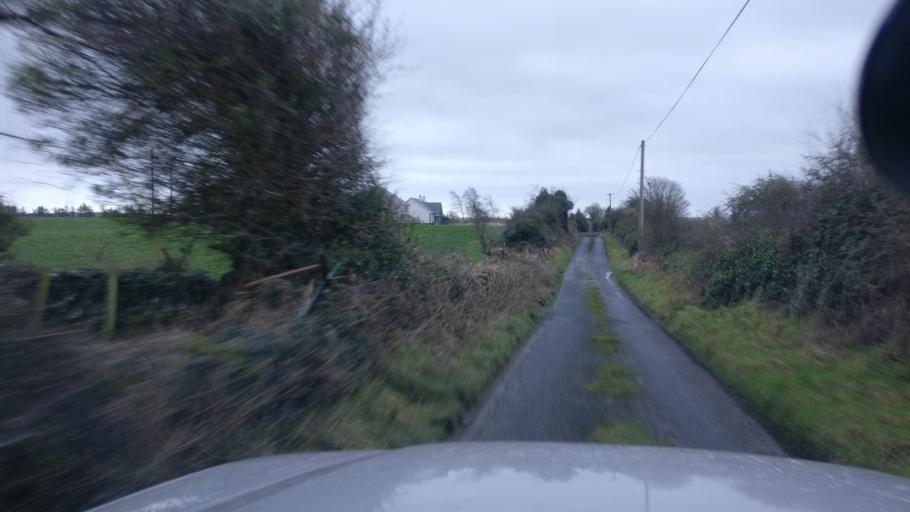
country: IE
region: Connaught
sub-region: County Galway
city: Loughrea
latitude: 53.2028
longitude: -8.6459
